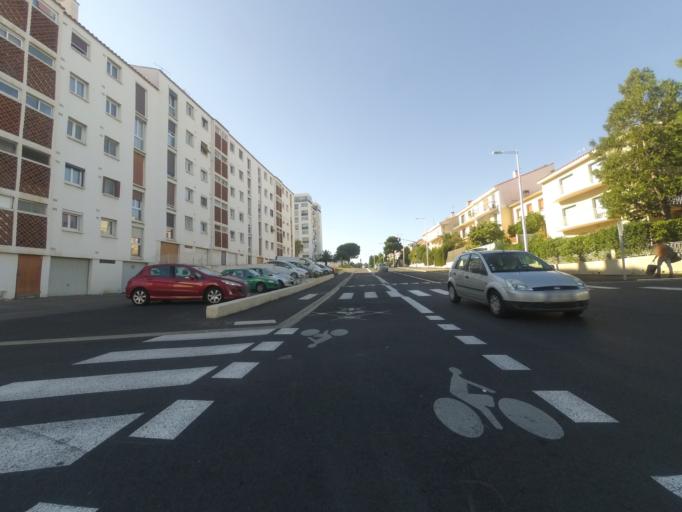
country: FR
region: Languedoc-Roussillon
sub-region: Departement des Pyrenees-Orientales
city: Perpignan
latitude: 42.6857
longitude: 2.9021
